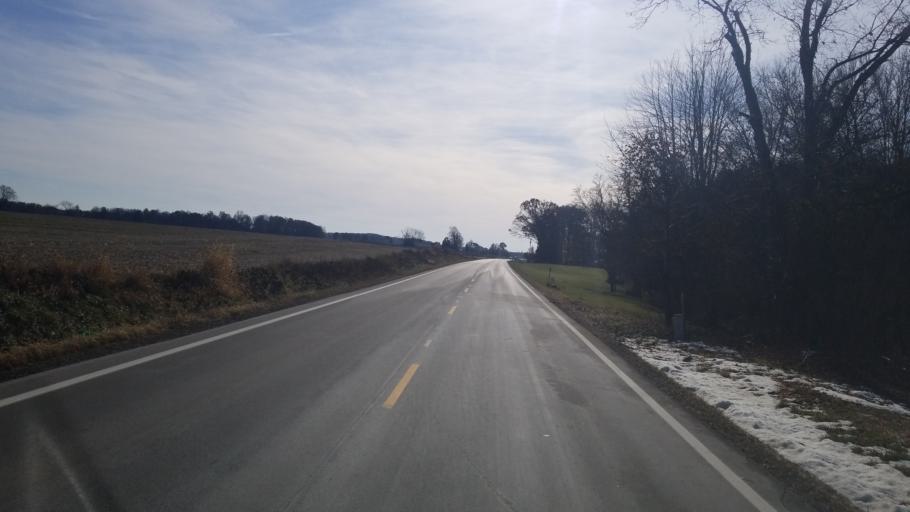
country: US
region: Ohio
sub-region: Huron County
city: Norwalk
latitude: 41.1964
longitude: -82.6363
